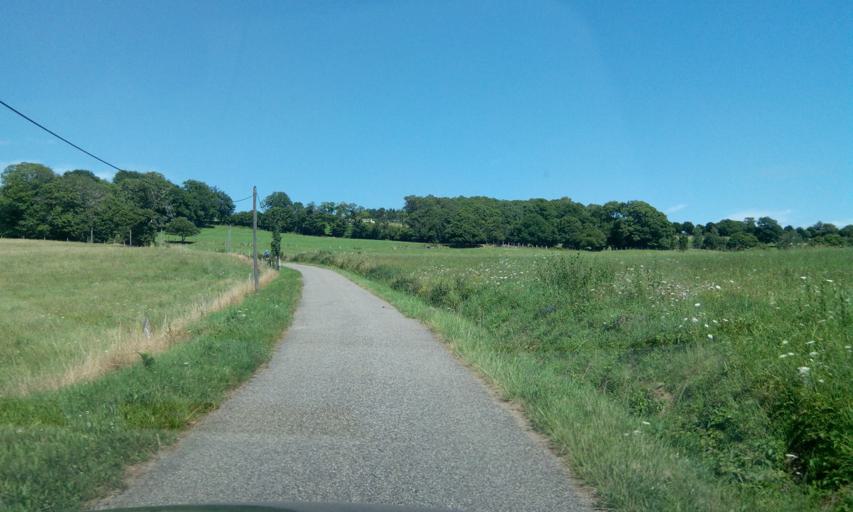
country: FR
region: Limousin
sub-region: Departement de la Correze
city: Beynat
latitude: 45.0794
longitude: 1.7754
